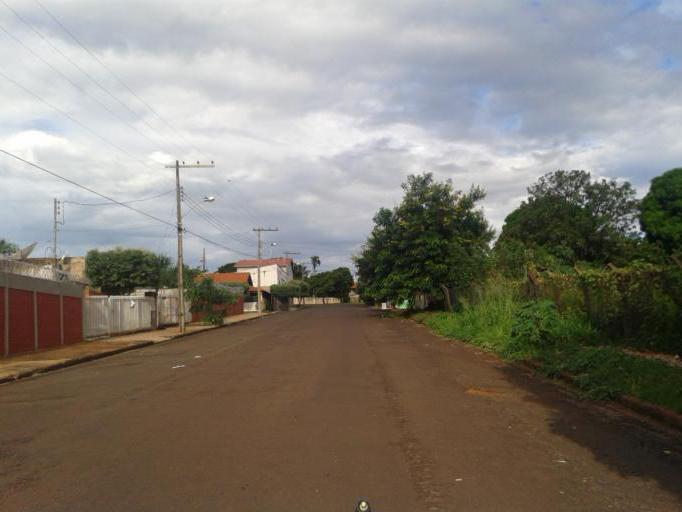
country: BR
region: Minas Gerais
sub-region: Ituiutaba
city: Ituiutaba
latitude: -18.9637
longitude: -49.4570
